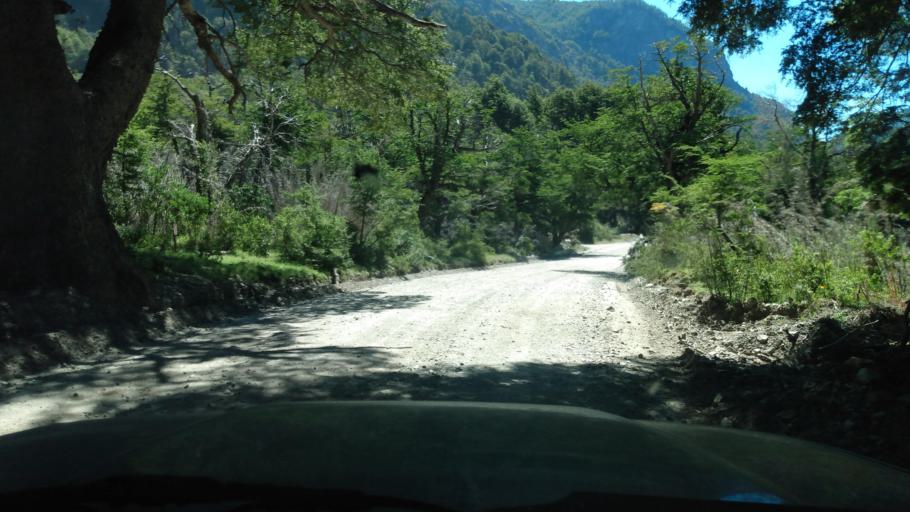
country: AR
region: Neuquen
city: Villa La Angostura
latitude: -40.6200
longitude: -71.6032
